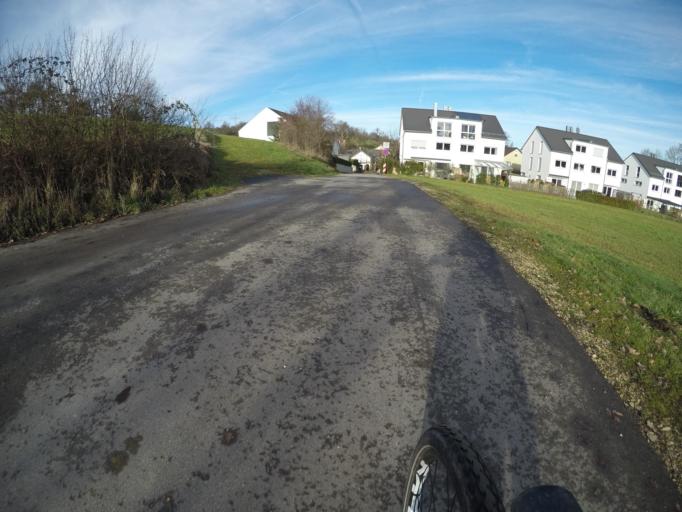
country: DE
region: Baden-Wuerttemberg
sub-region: Regierungsbezirk Stuttgart
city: Dettingen unter Teck
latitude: 48.6105
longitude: 9.4474
